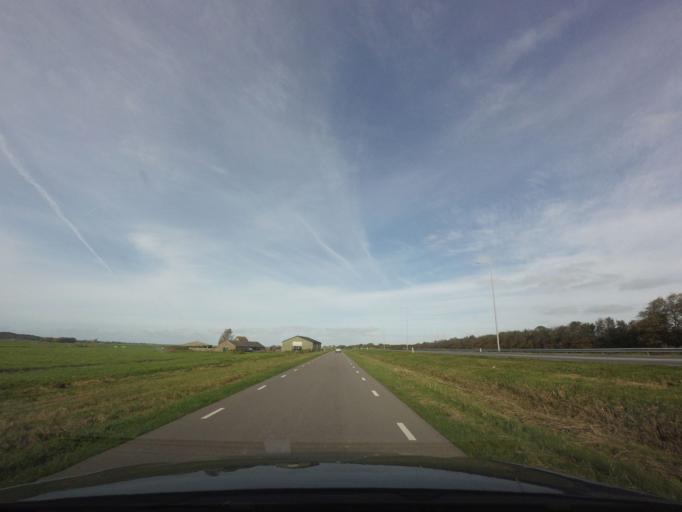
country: NL
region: North Holland
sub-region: Gemeente Schagen
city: Harenkarspel
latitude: 52.7141
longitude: 4.7098
